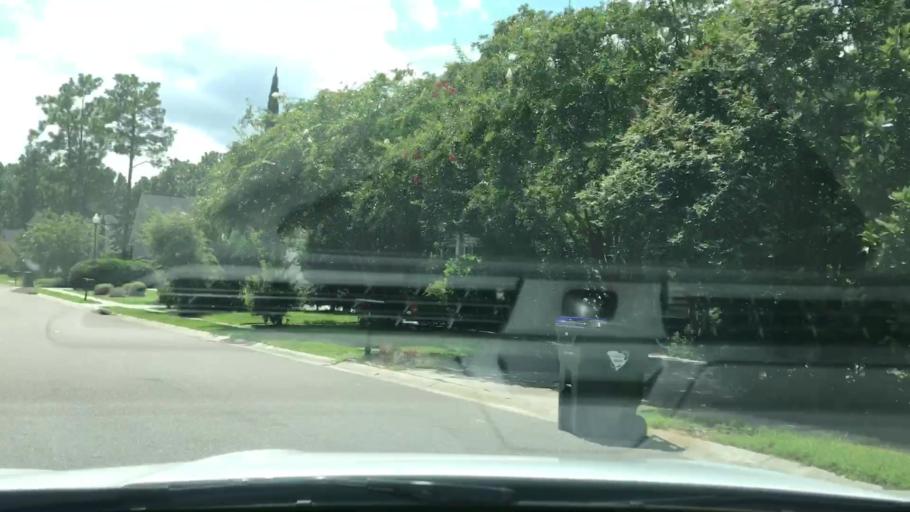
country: US
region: South Carolina
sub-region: Dorchester County
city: Summerville
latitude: 33.0377
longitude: -80.2249
